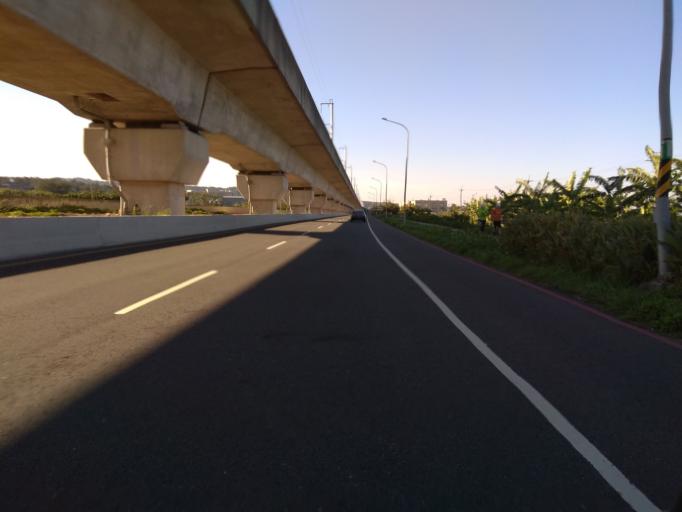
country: TW
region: Taiwan
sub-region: Hsinchu
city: Zhubei
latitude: 24.9015
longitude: 121.0823
